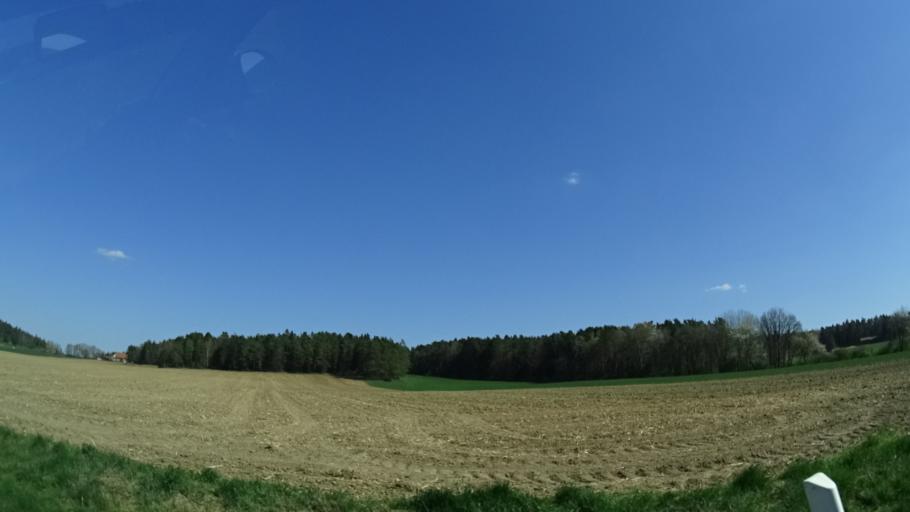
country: DE
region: Bavaria
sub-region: Upper Palatinate
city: Illschwang
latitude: 49.4953
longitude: 11.6531
